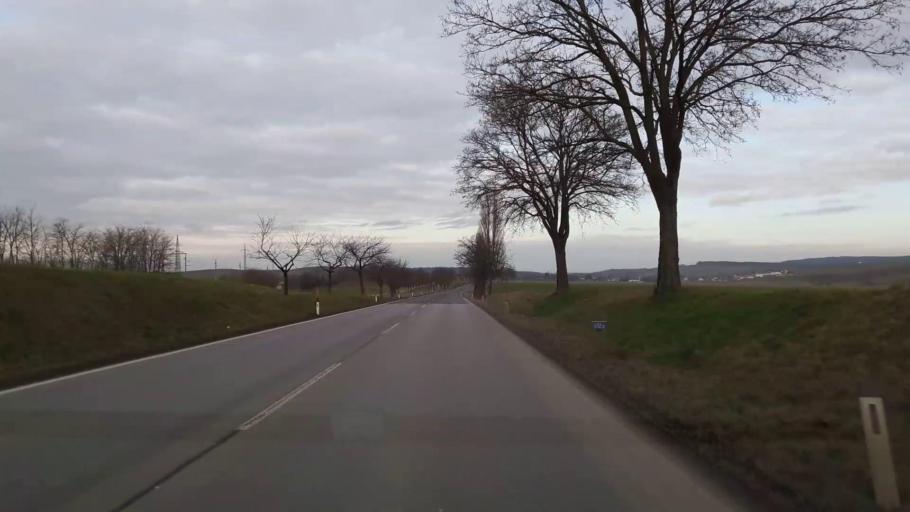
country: AT
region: Lower Austria
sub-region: Politischer Bezirk Mistelbach
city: Mistelbach
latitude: 48.5883
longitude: 16.5534
